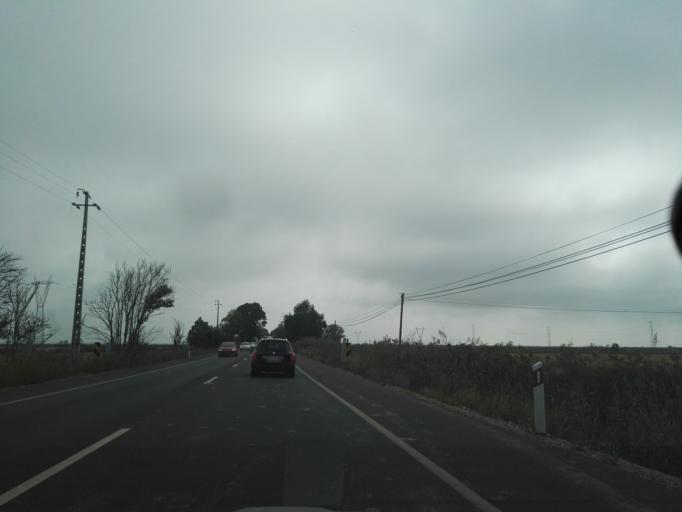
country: PT
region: Lisbon
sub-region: Vila Franca de Xira
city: Vila Franca de Xira
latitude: 38.9483
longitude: -8.9642
